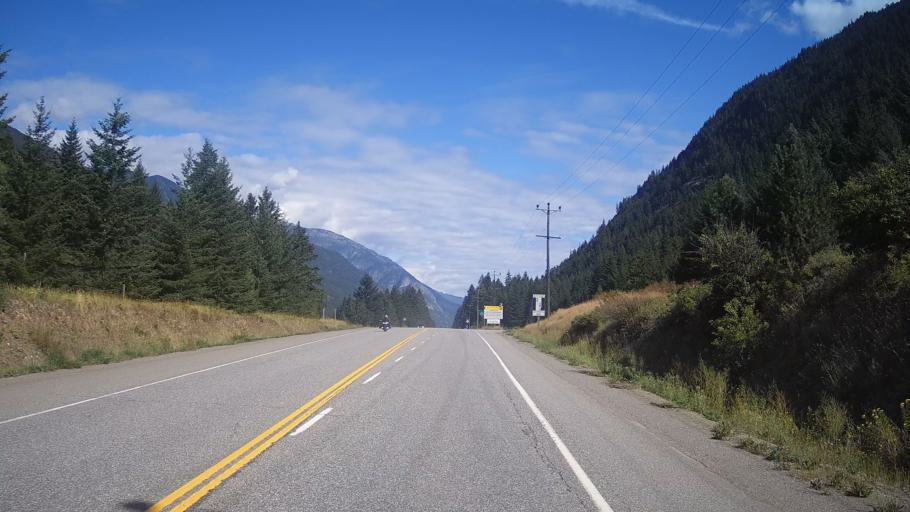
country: CA
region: British Columbia
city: Hope
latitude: 50.0349
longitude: -121.5324
